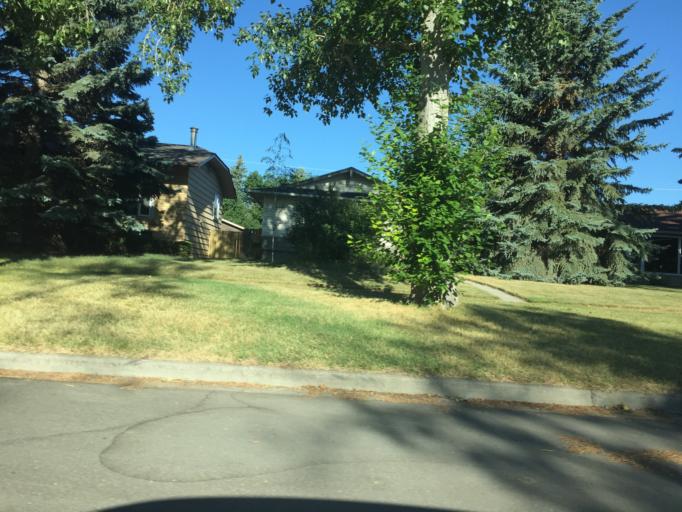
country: CA
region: Alberta
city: Calgary
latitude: 50.9381
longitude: -114.0645
